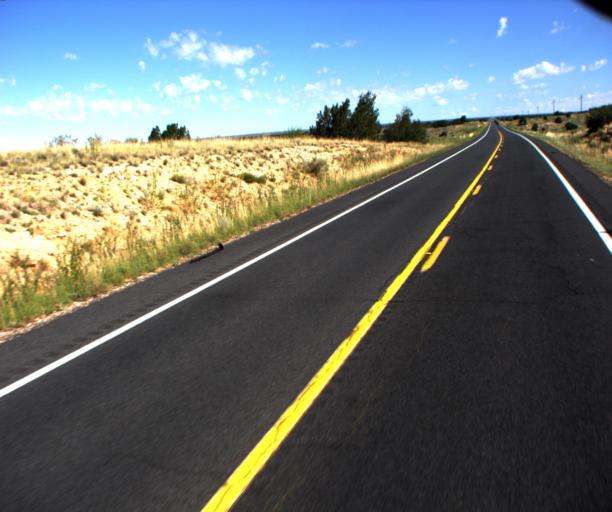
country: US
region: Arizona
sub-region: Coconino County
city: Grand Canyon Village
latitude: 35.7127
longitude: -112.1313
